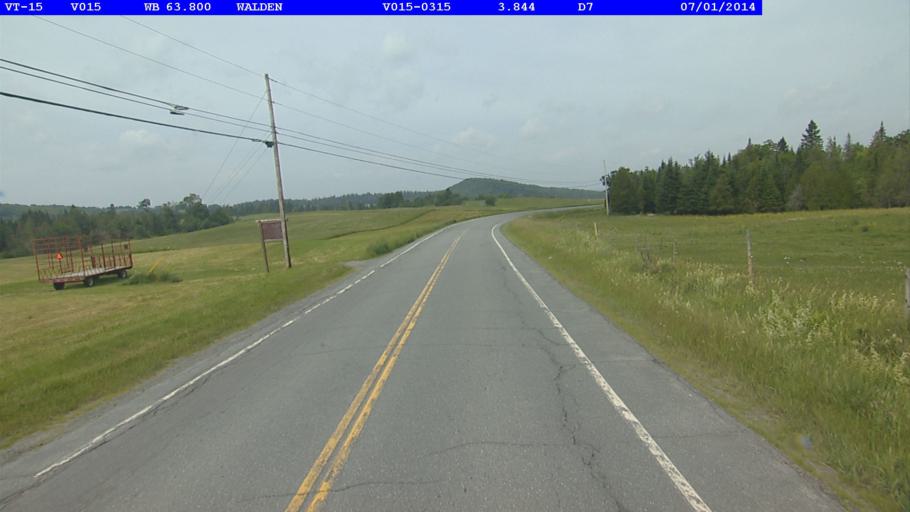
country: US
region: Vermont
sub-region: Caledonia County
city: Hardwick
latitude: 44.4491
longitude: -72.2503
